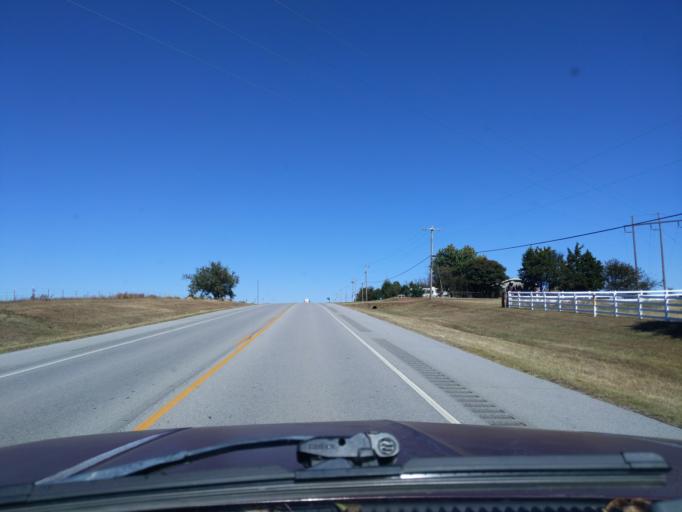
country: US
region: Oklahoma
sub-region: Creek County
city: Bristow
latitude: 35.7828
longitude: -96.3871
